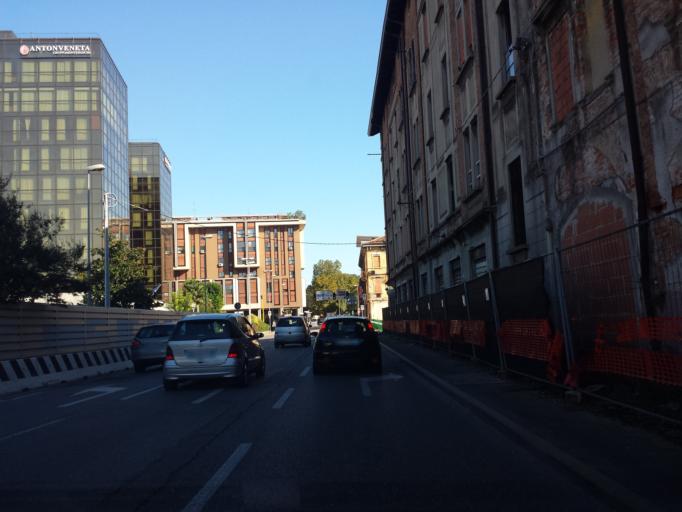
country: IT
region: Veneto
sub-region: Provincia di Padova
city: Padova
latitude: 45.4131
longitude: 11.8814
